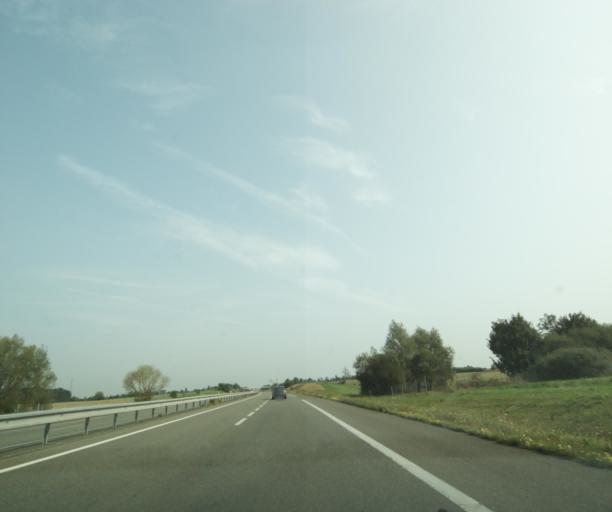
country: FR
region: Pays de la Loire
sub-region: Departement de la Sarthe
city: Montbizot
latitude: 48.1883
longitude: 0.1706
